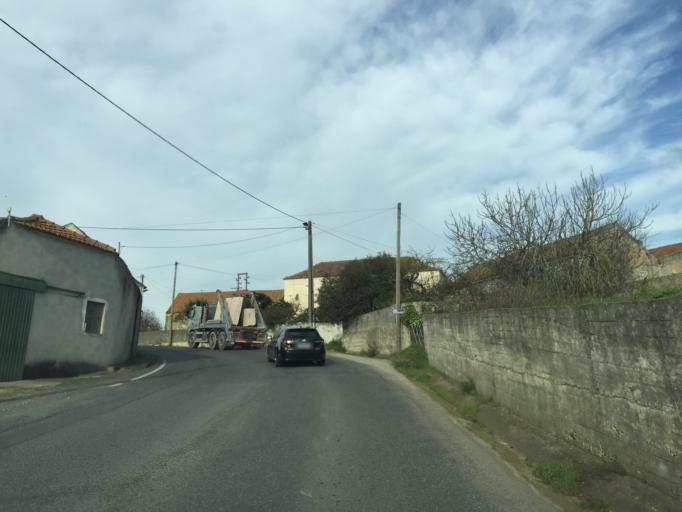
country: PT
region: Lisbon
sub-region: Sintra
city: Pero Pinheiro
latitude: 38.8616
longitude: -9.3092
